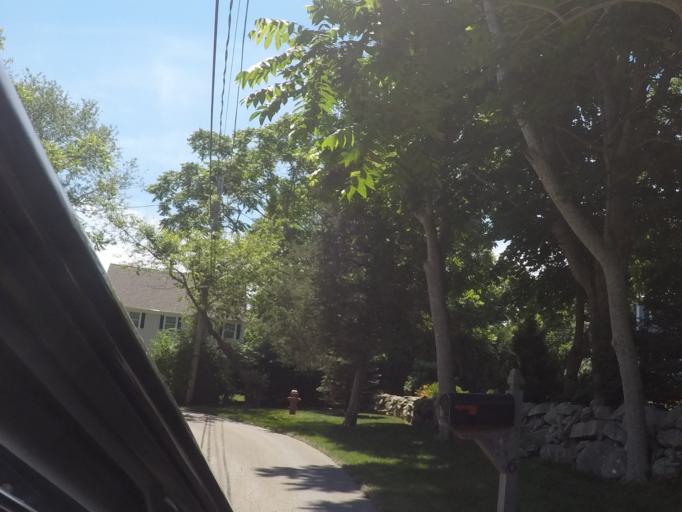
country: US
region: Massachusetts
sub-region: Bristol County
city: Bliss Corner
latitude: 41.5544
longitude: -70.9529
